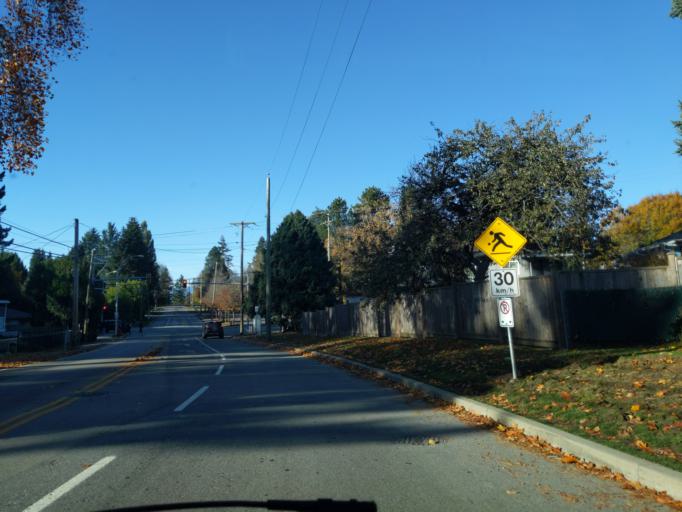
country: CA
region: British Columbia
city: New Westminster
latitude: 49.1911
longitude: -122.8627
